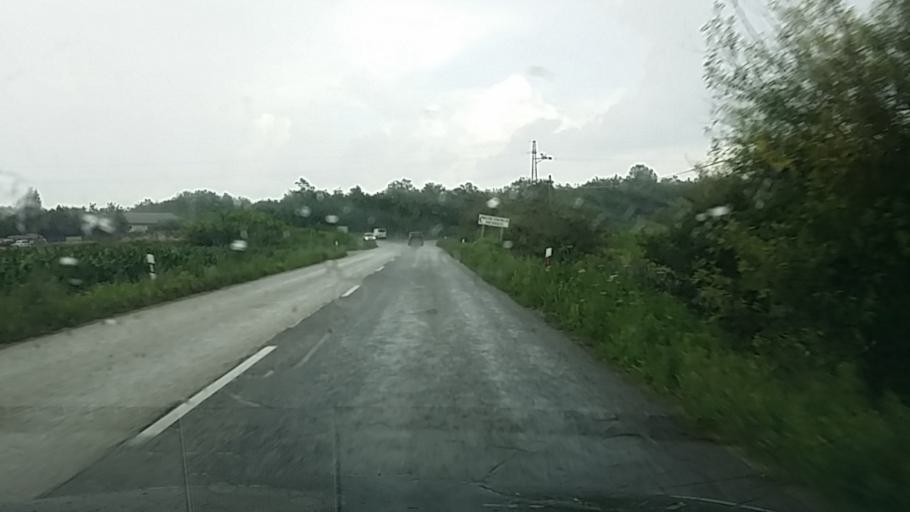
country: HU
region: Pest
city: Ocsa
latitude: 47.3011
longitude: 19.2632
